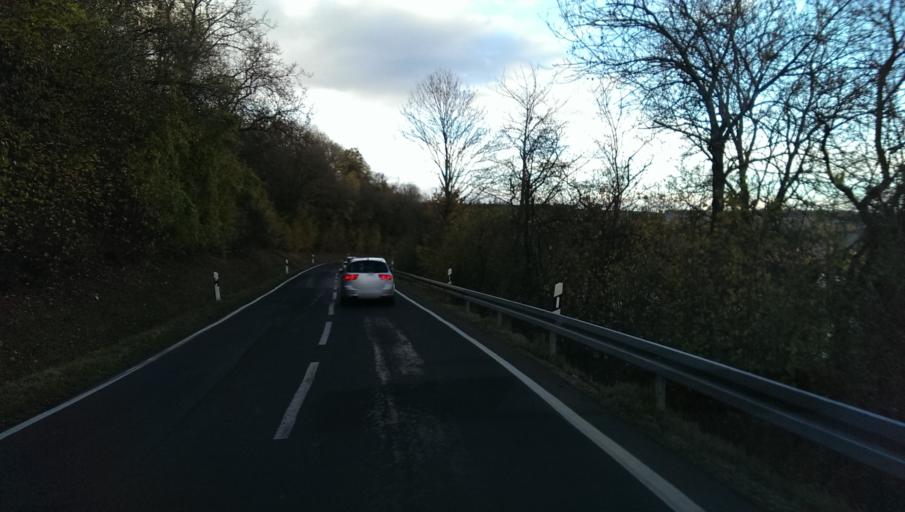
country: DE
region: Bavaria
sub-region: Regierungsbezirk Unterfranken
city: Thungen
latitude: 49.9361
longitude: 9.8567
